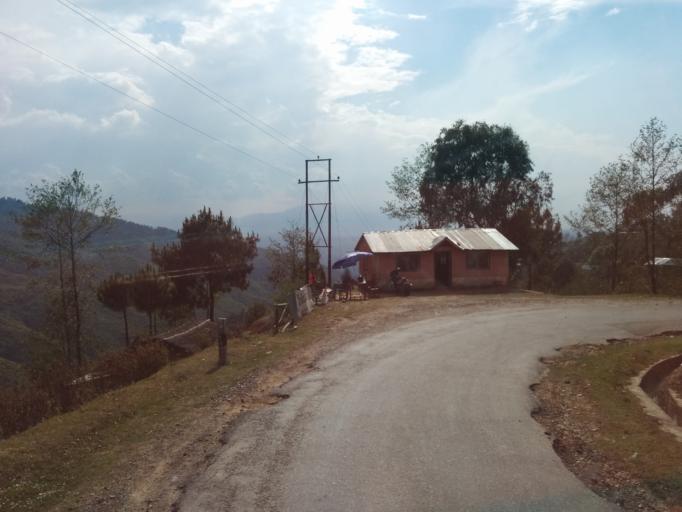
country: NP
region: Central Region
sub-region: Bagmati Zone
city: Nagarkot
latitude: 27.7092
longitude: 85.5062
